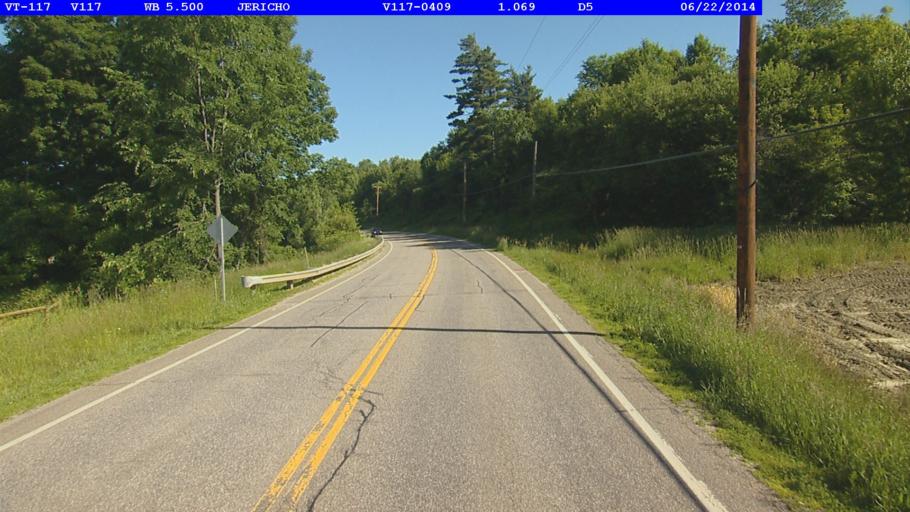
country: US
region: Vermont
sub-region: Chittenden County
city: Jericho
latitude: 44.4591
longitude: -73.0199
